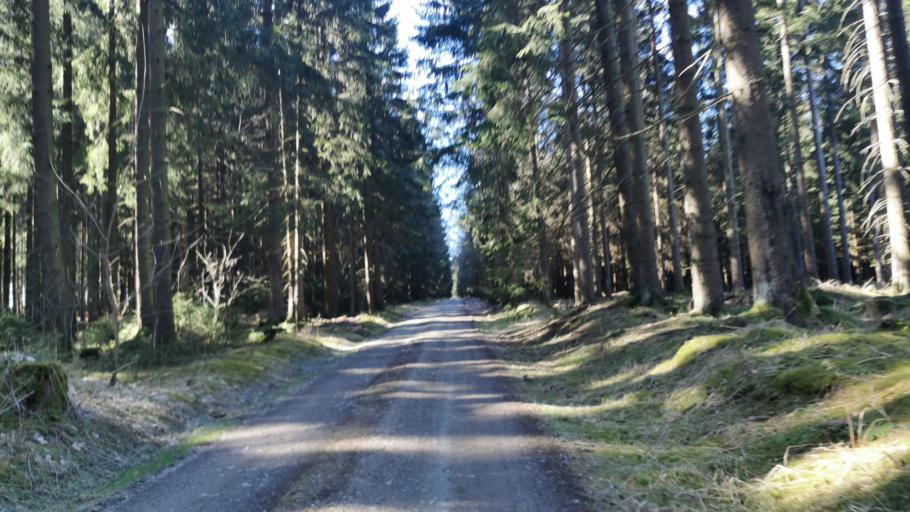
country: DE
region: Thuringia
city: Wurzbach
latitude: 50.4373
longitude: 11.4990
